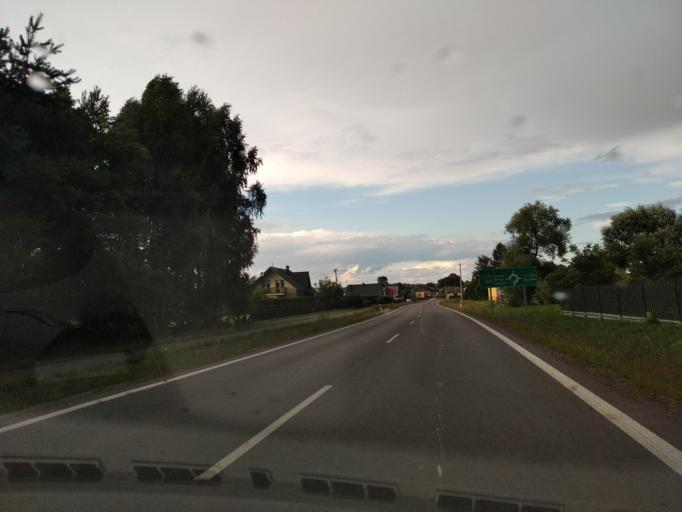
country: PL
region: Subcarpathian Voivodeship
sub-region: Powiat kolbuszowski
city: Kolbuszowa
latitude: 50.2303
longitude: 21.7846
